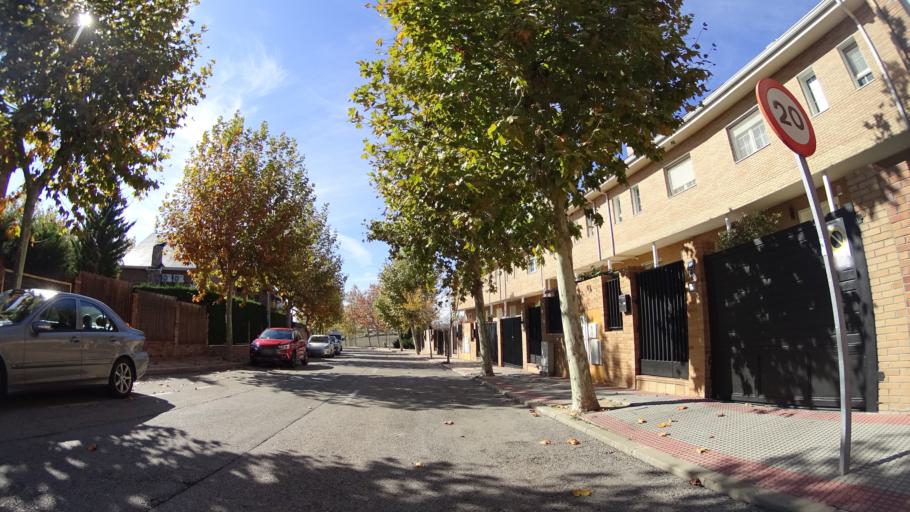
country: ES
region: Madrid
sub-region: Provincia de Madrid
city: Villanueva del Pardillo
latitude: 40.5007
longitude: -3.9695
